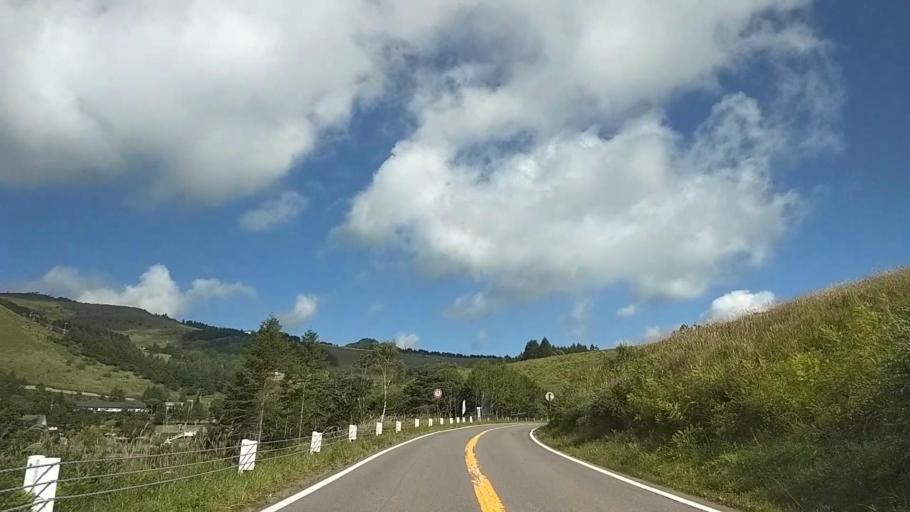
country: JP
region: Nagano
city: Suwa
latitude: 36.0971
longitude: 138.2156
